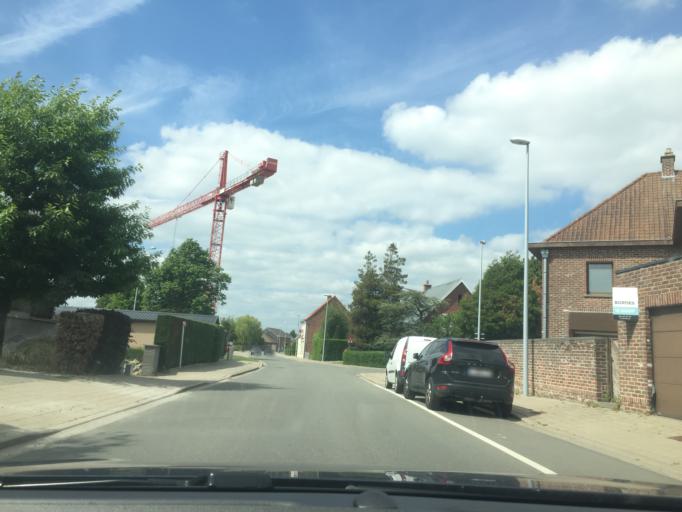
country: BE
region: Flanders
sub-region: Provincie West-Vlaanderen
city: Izegem
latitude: 50.9103
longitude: 3.2302
